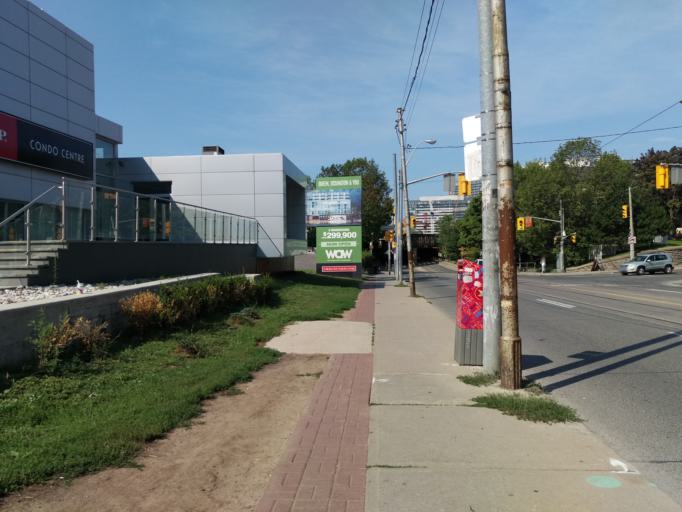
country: CA
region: Ontario
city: Toronto
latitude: 43.6411
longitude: -79.4169
